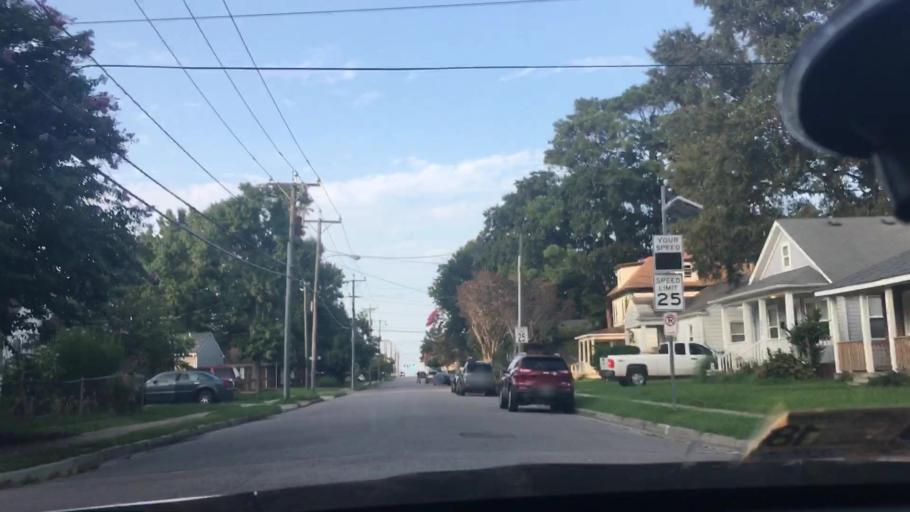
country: US
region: Virginia
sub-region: City of Norfolk
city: Norfolk
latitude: 36.9442
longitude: -76.2439
